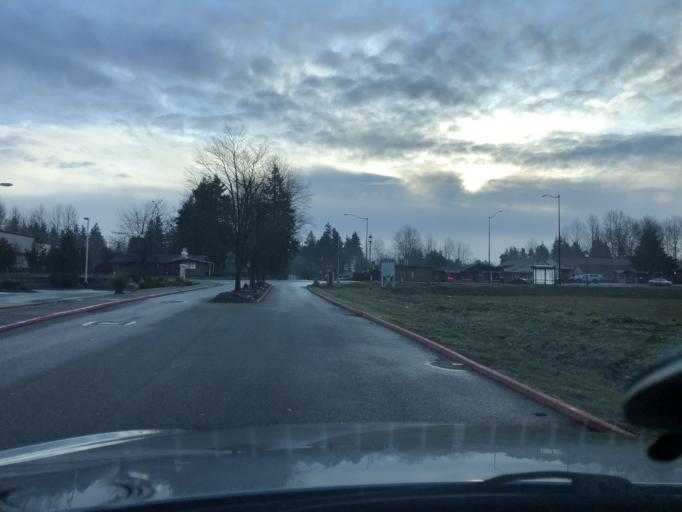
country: US
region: Washington
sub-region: Pierce County
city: Edgewood
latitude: 47.2450
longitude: -122.2951
